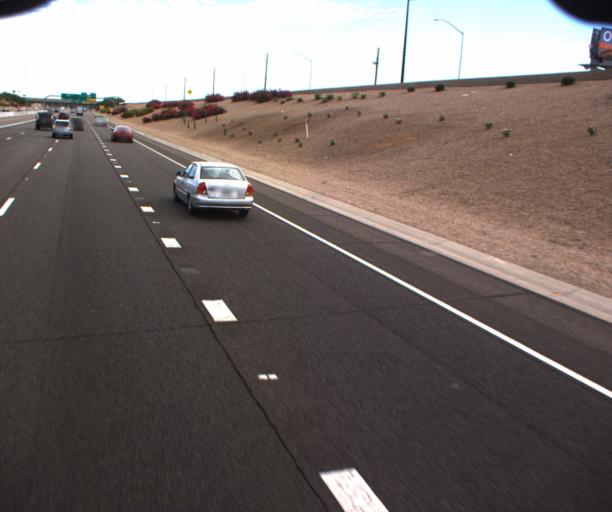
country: US
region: Arizona
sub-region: Maricopa County
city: Chandler
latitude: 33.2916
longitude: -111.9105
